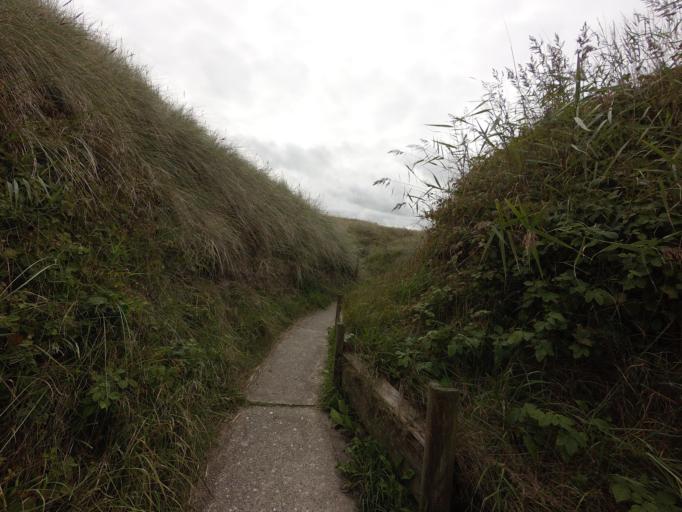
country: DK
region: North Denmark
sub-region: Hjorring Kommune
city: Hirtshals
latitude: 57.5835
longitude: 9.9379
